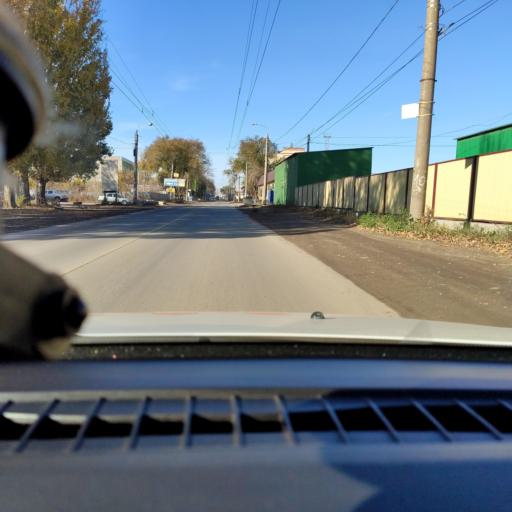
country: RU
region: Samara
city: Samara
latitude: 53.1972
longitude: 50.2700
